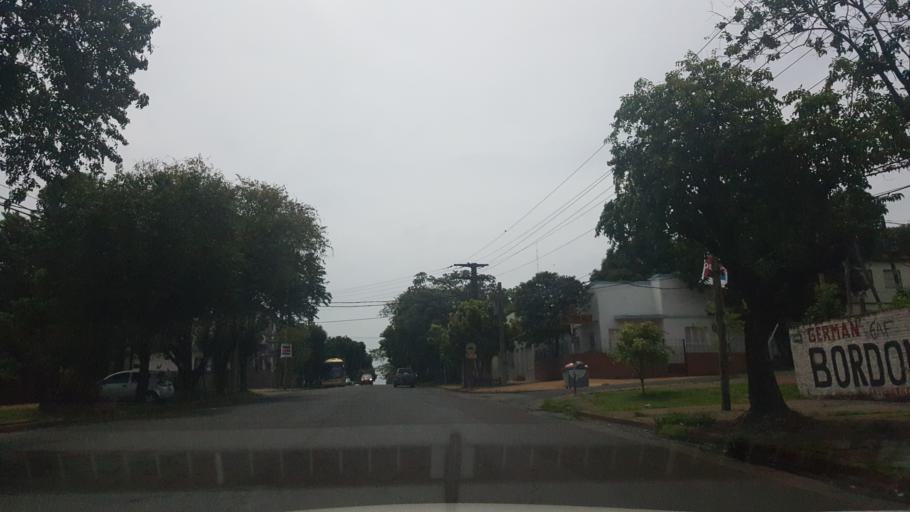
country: AR
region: Misiones
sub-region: Departamento de Capital
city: Posadas
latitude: -27.3578
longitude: -55.9000
